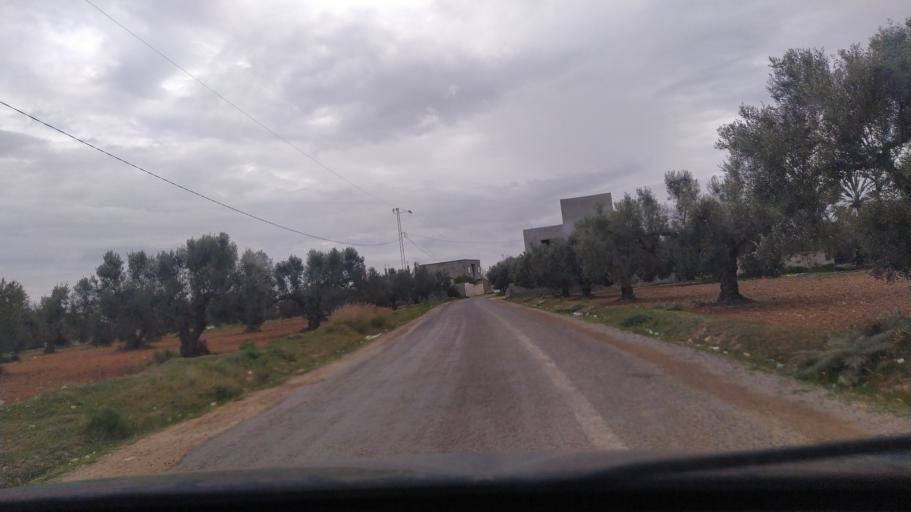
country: TN
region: Al Munastir
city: Sidi Bin Nur
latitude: 35.5127
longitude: 10.9657
